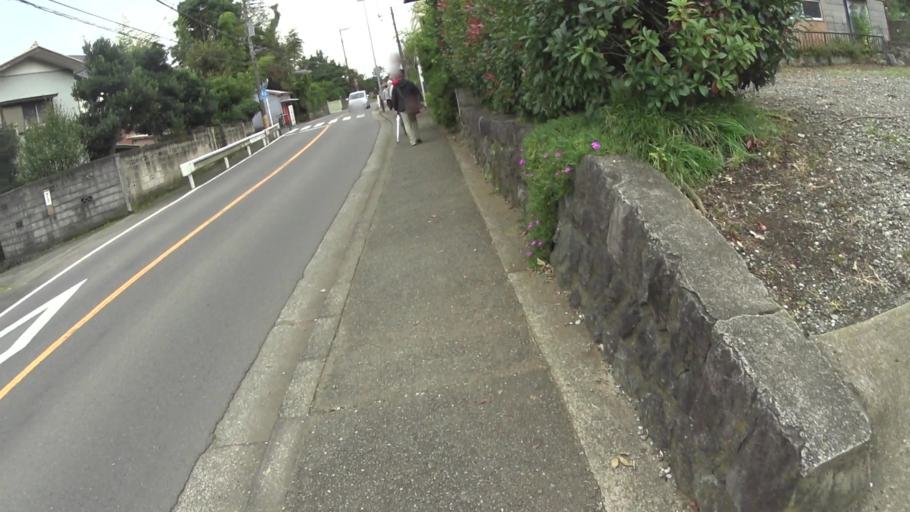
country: JP
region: Kanagawa
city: Hadano
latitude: 35.3949
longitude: 139.2233
